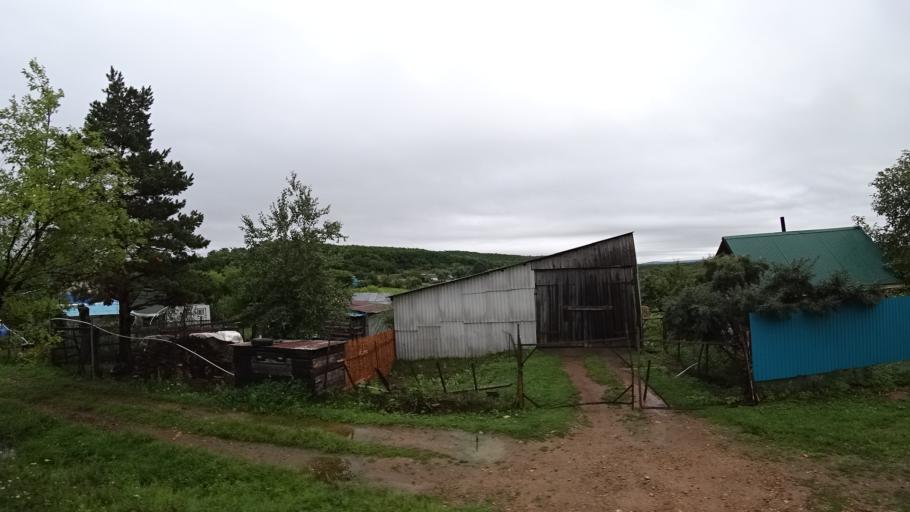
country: RU
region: Primorskiy
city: Monastyrishche
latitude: 44.2580
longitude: 132.4143
